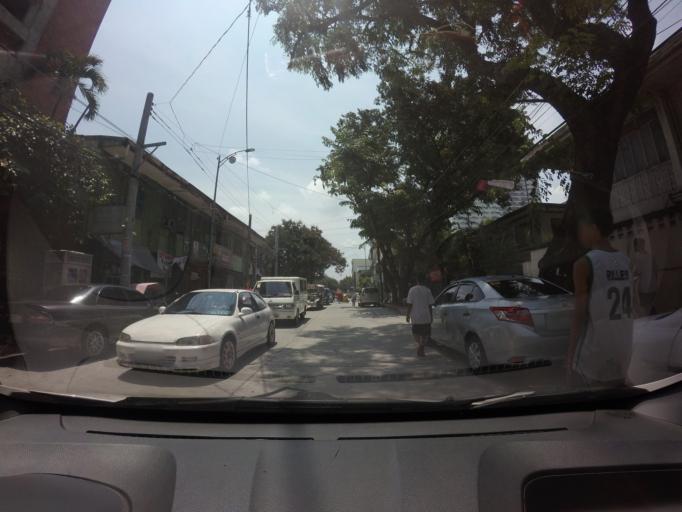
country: PH
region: Metro Manila
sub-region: City of Manila
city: Quiapo
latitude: 14.5818
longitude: 120.9949
